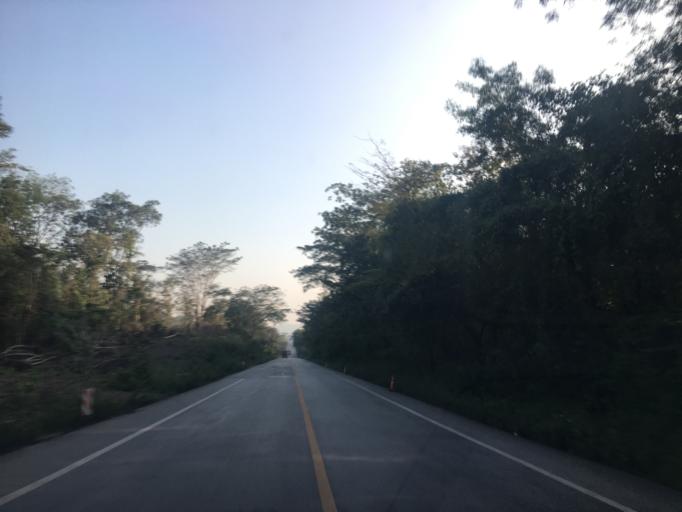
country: TH
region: Lampang
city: Ngao
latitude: 18.6573
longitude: 100.0176
